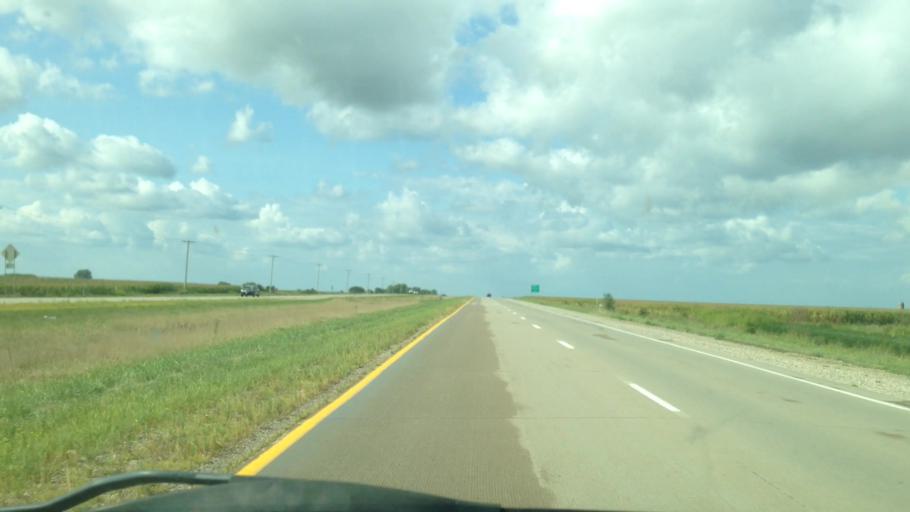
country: US
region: Iowa
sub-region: Henry County
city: Mount Pleasant
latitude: 40.7467
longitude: -91.5637
